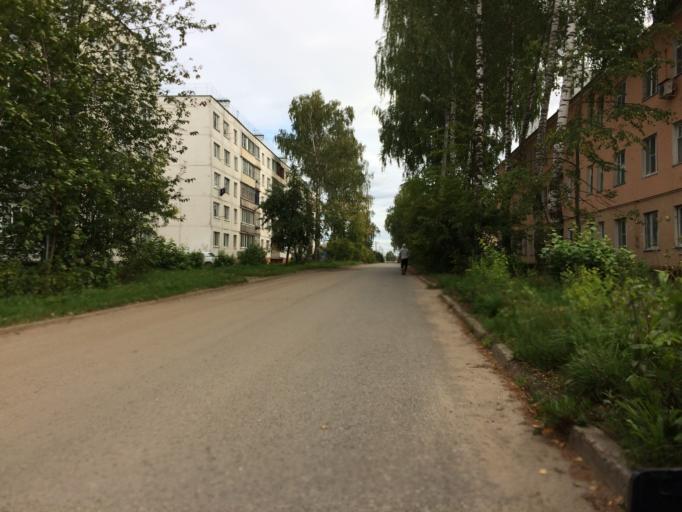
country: RU
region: Mariy-El
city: Yoshkar-Ola
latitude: 56.6573
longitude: 47.9797
